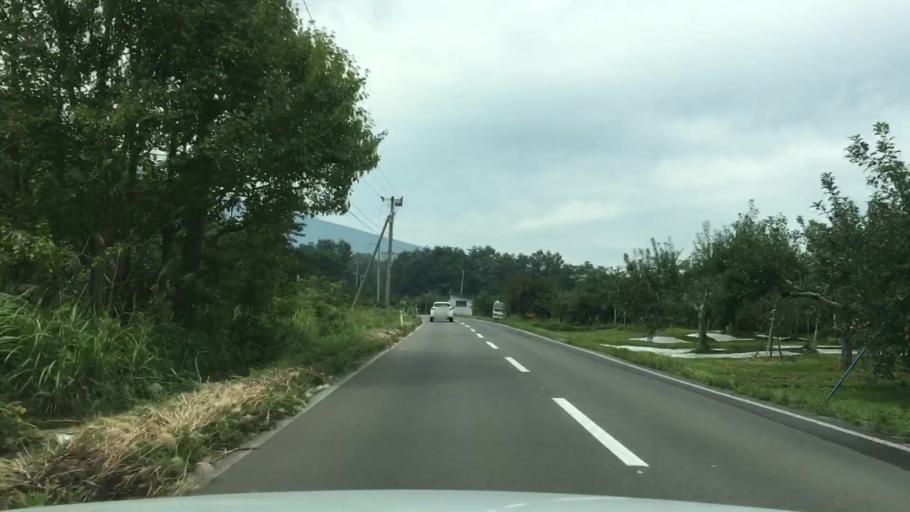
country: JP
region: Aomori
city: Hirosaki
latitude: 40.6683
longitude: 140.3931
